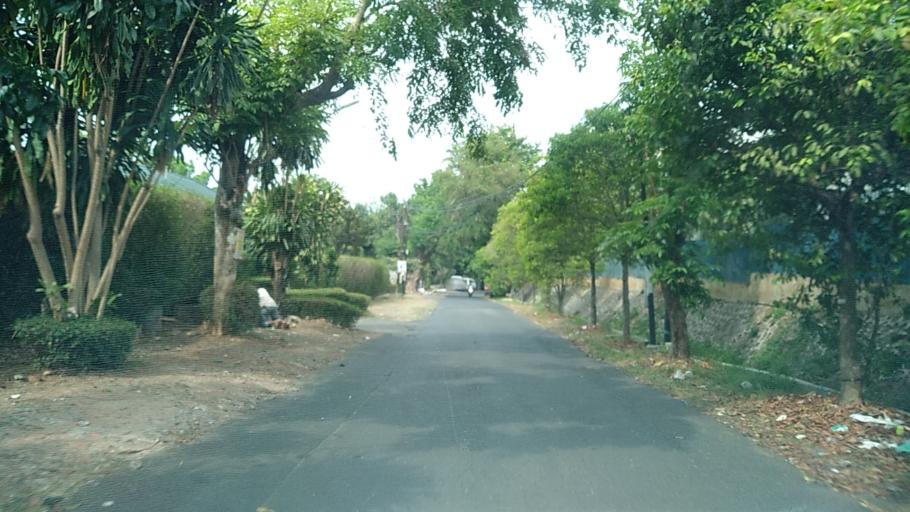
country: ID
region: Central Java
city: Semarang
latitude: -7.0074
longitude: 110.4190
